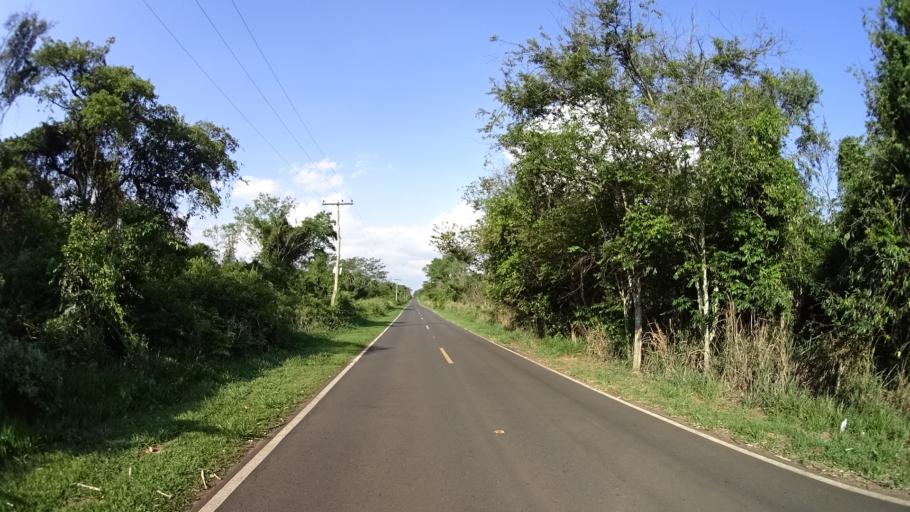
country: BR
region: Sao Paulo
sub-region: Urupes
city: Urupes
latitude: -21.3801
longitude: -49.4867
